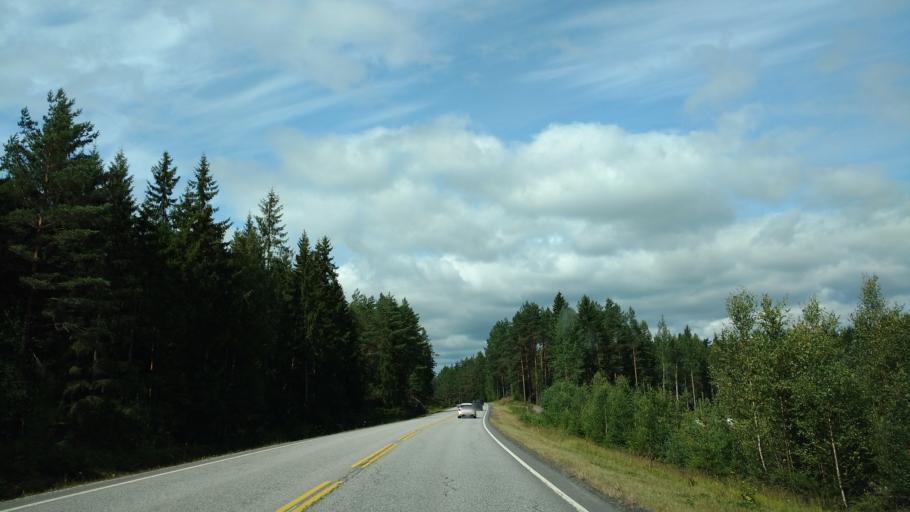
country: FI
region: Varsinais-Suomi
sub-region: Salo
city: Saerkisalo
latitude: 60.1768
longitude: 22.9152
